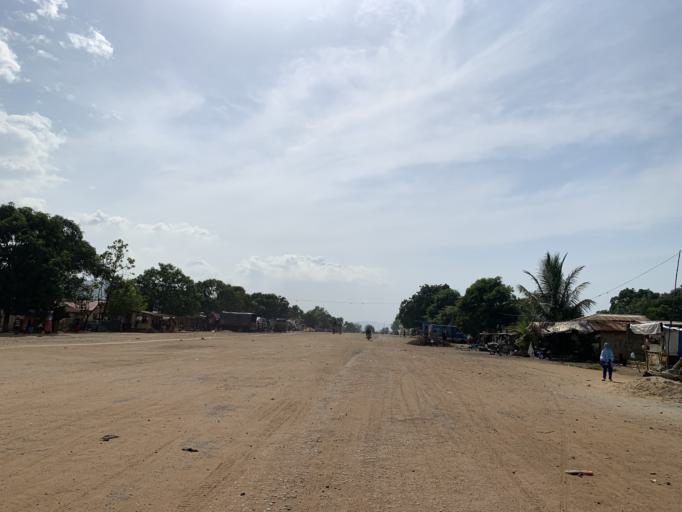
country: SL
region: Western Area
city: Waterloo
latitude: 8.3396
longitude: -13.0466
